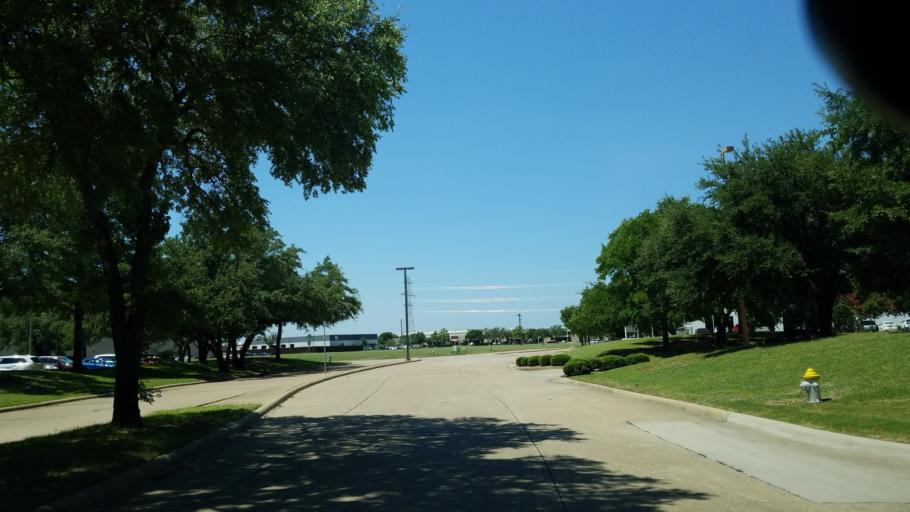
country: US
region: Texas
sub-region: Dallas County
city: Carrollton
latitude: 32.9603
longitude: -96.9170
